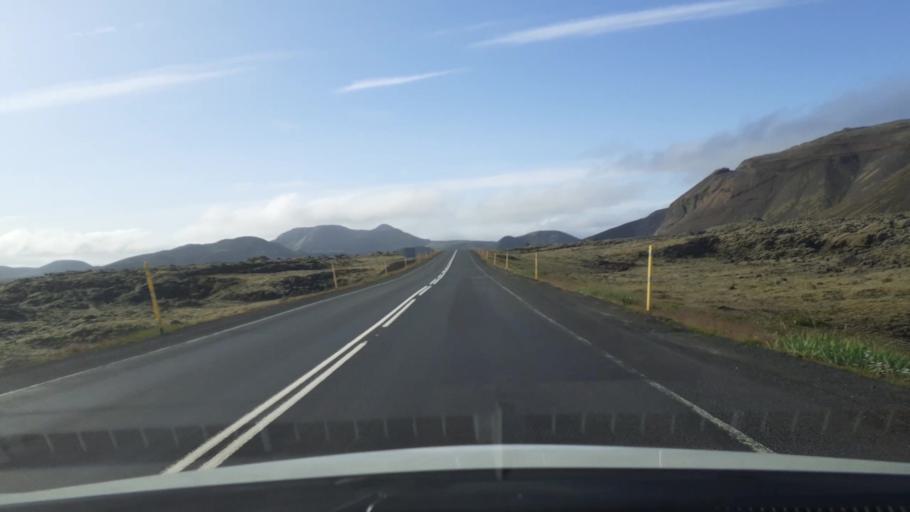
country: IS
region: South
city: THorlakshoefn
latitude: 64.0333
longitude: -21.4556
